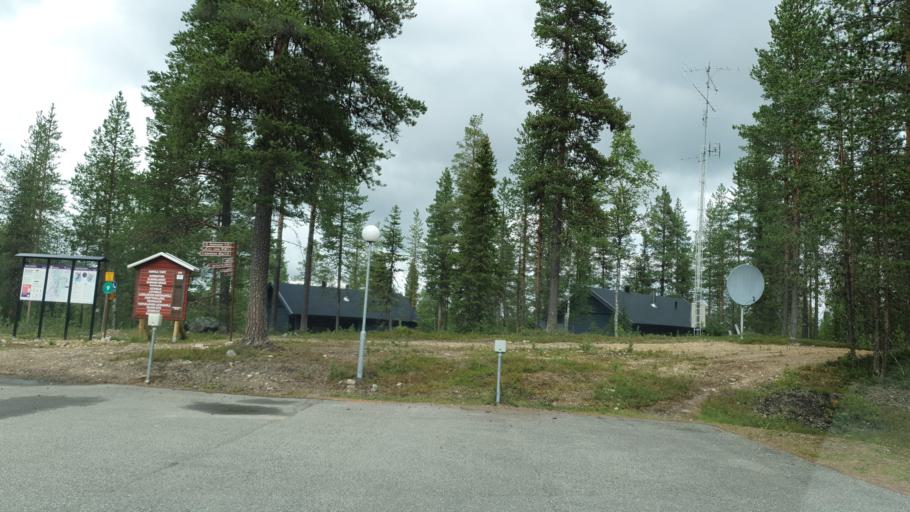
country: FI
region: Lapland
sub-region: Tunturi-Lappi
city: Kolari
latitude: 67.5306
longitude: 24.2577
